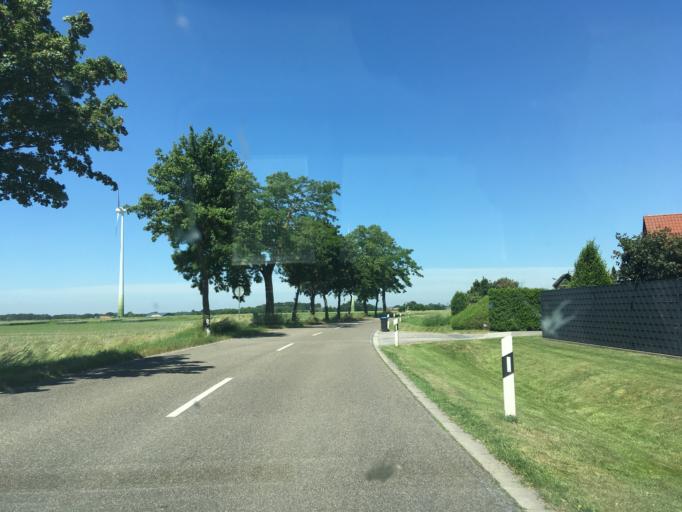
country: DE
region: North Rhine-Westphalia
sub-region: Regierungsbezirk Munster
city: Raesfeld
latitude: 51.7752
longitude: 6.8298
